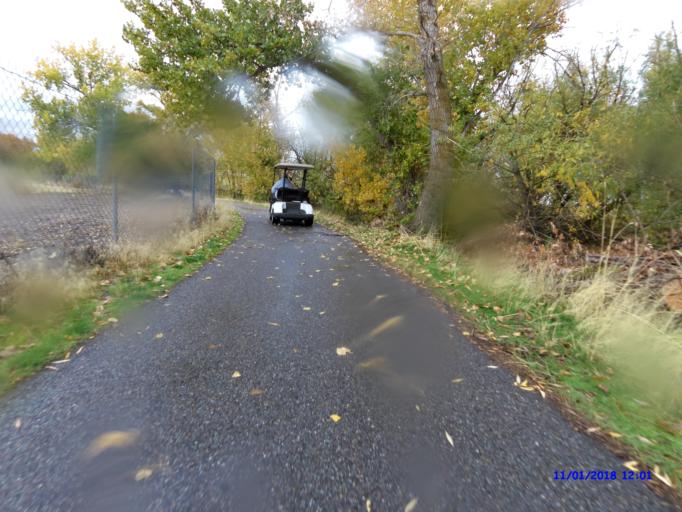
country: US
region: Utah
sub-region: Weber County
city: Ogden
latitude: 41.2315
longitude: -112.0017
